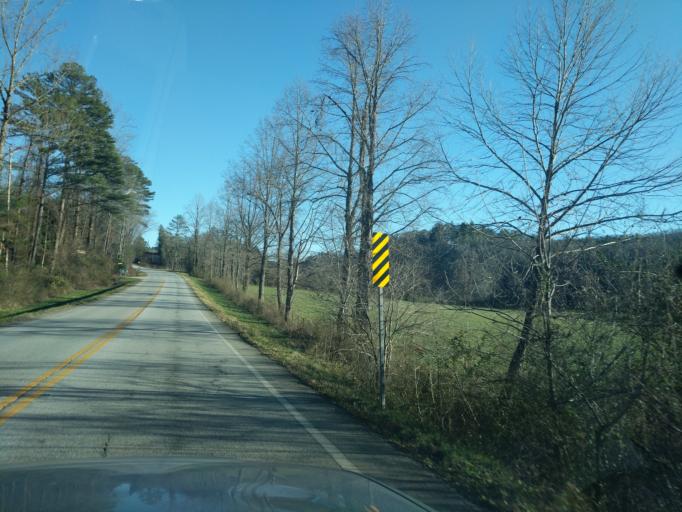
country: US
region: Georgia
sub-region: Rabun County
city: Clayton
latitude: 34.8487
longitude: -83.3602
